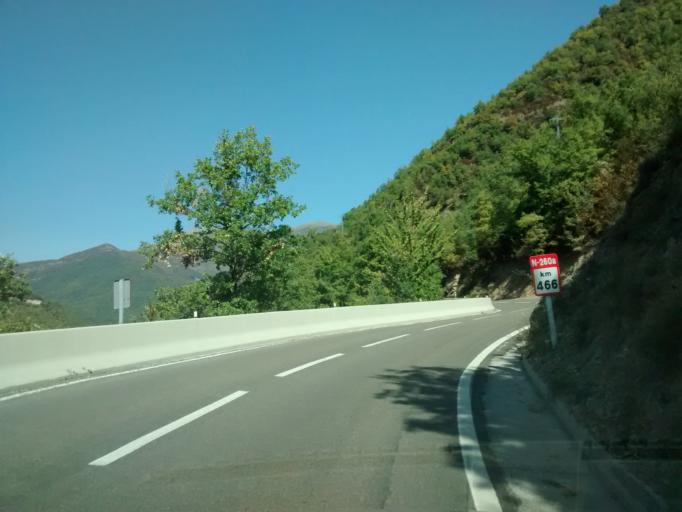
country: ES
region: Aragon
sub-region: Provincia de Huesca
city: Fiscal
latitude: 42.5172
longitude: -0.1280
